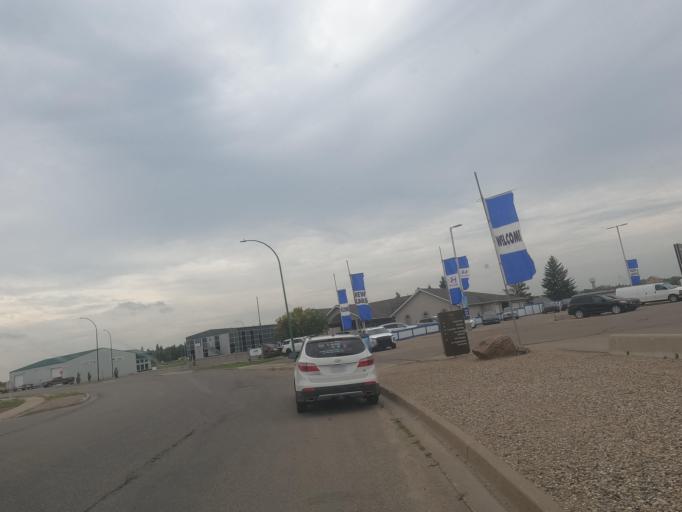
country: CA
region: Saskatchewan
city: Yorkton
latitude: 51.2074
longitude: -102.4467
